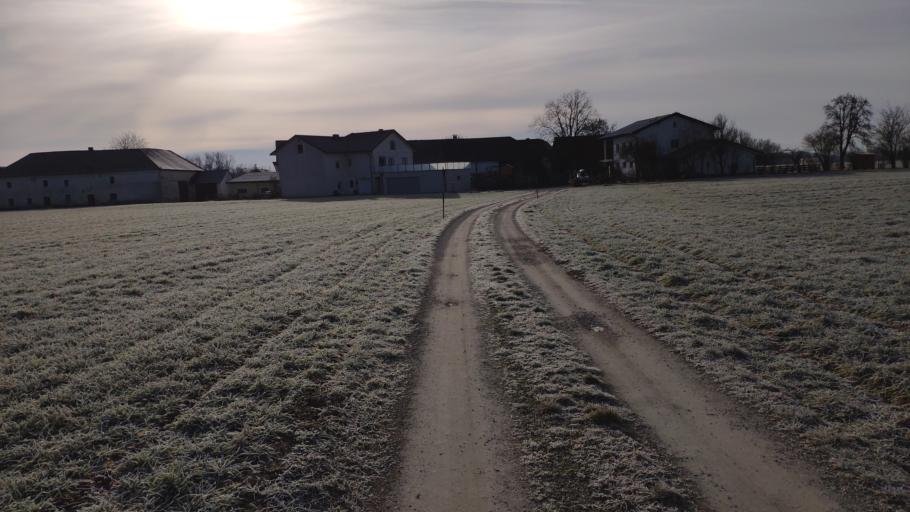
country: AT
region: Upper Austria
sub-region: Politischer Bezirk Perg
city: Perg
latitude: 48.2520
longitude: 14.5672
